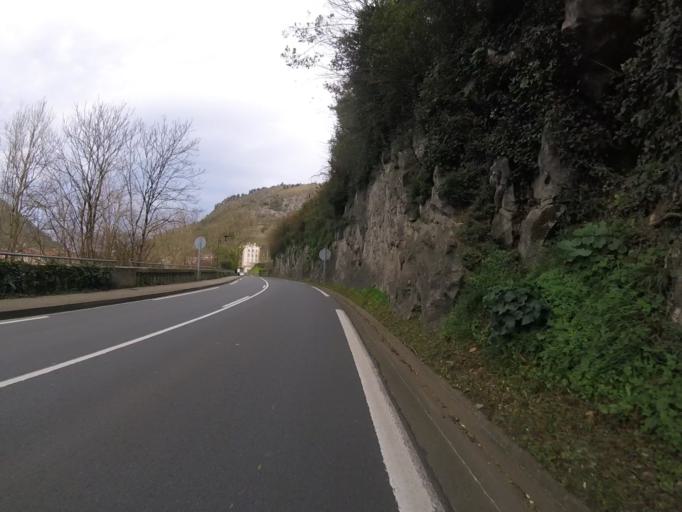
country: ES
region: Basque Country
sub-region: Provincia de Guipuzcoa
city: Cestona
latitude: 43.2354
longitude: -2.2548
